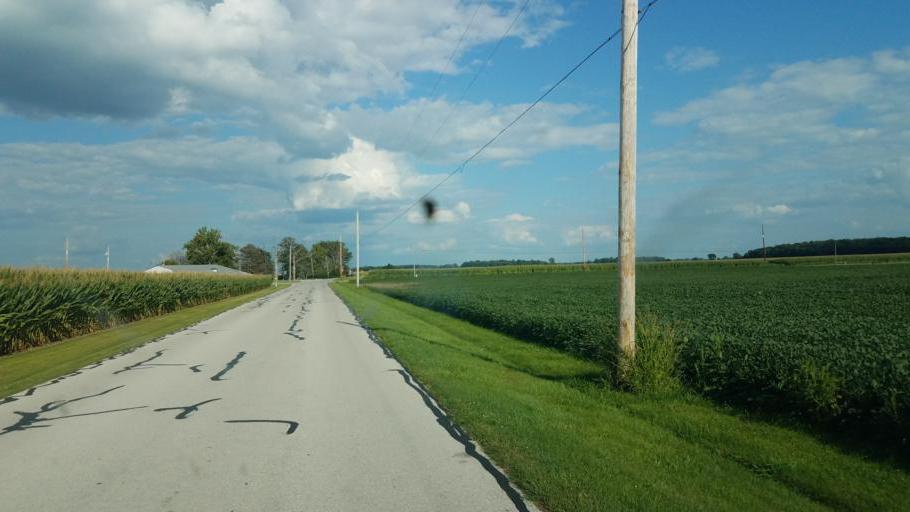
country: US
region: Ohio
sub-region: Wood County
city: Bowling Green
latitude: 41.3630
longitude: -83.5736
